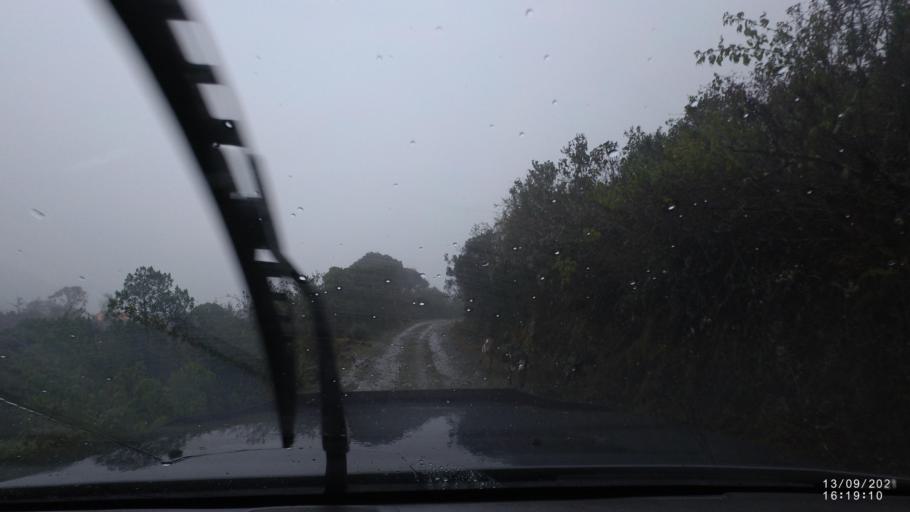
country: BO
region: Cochabamba
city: Colomi
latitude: -17.2700
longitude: -65.7052
